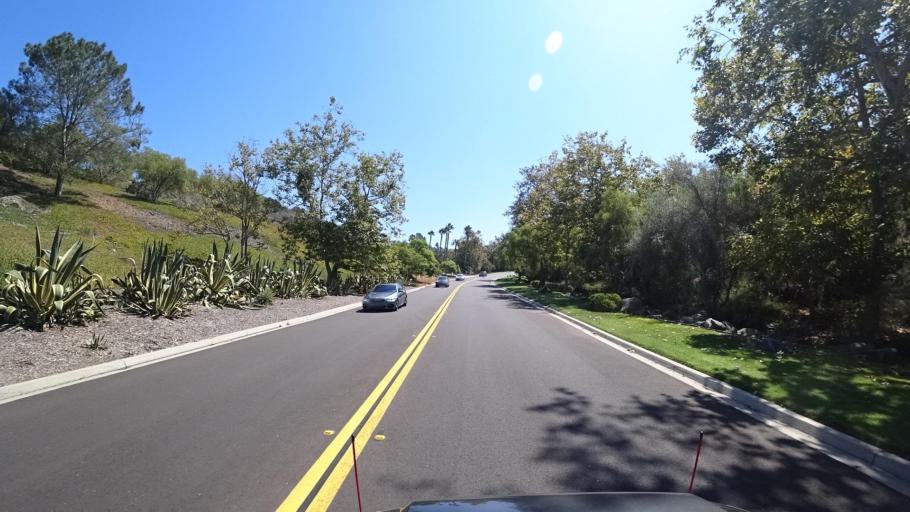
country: US
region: California
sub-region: San Diego County
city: Fairbanks Ranch
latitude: 32.9891
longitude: -117.1936
